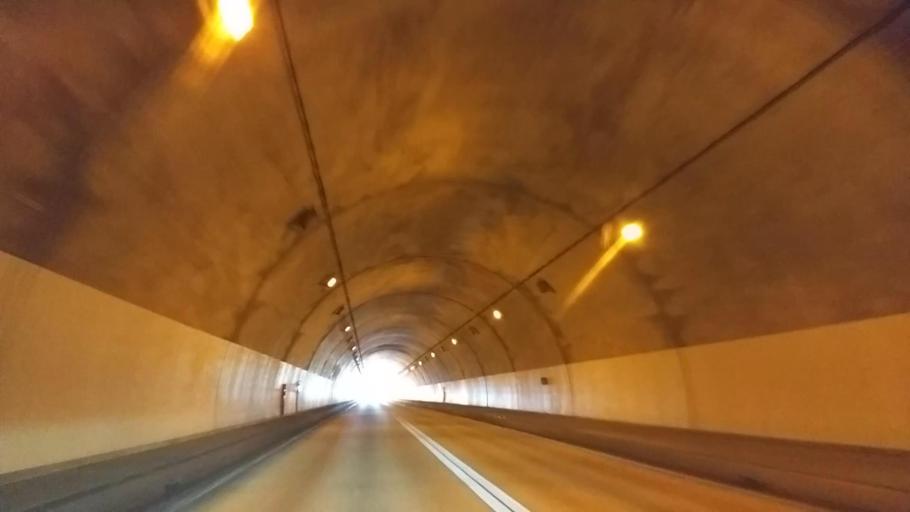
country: JP
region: Tochigi
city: Imaichi
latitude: 36.8531
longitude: 139.7241
